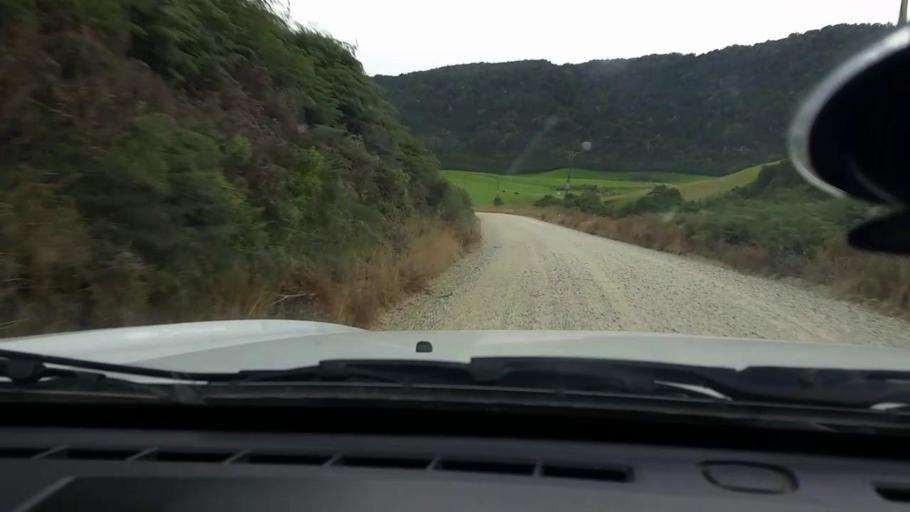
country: NZ
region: Otago
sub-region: Clutha District
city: Papatowai
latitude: -46.4625
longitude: 169.1227
